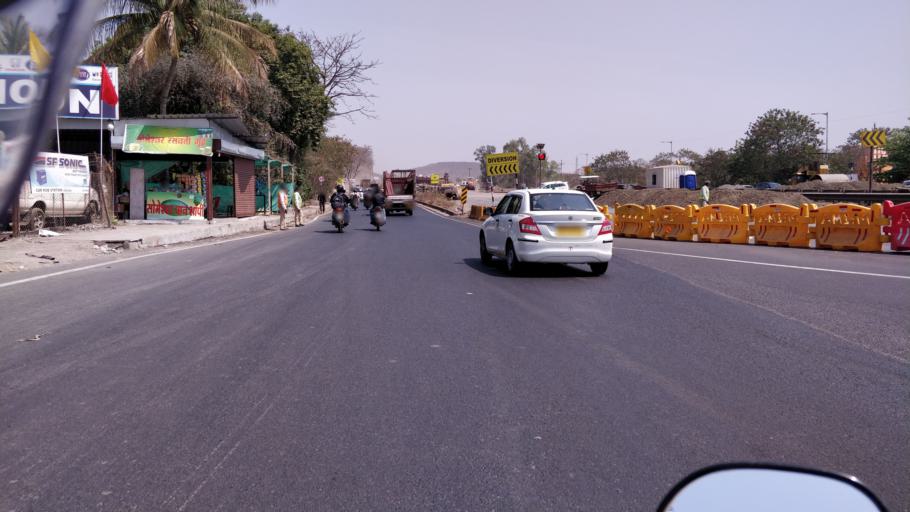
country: IN
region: Maharashtra
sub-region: Pune Division
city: Shivaji Nagar
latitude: 18.5319
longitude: 73.7795
